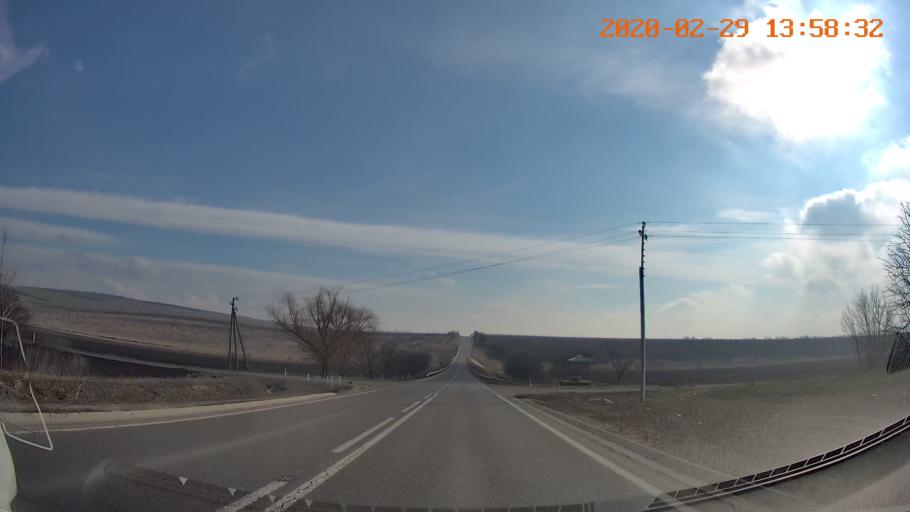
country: MD
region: Floresti
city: Leninskiy
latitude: 47.7747
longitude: 28.4587
